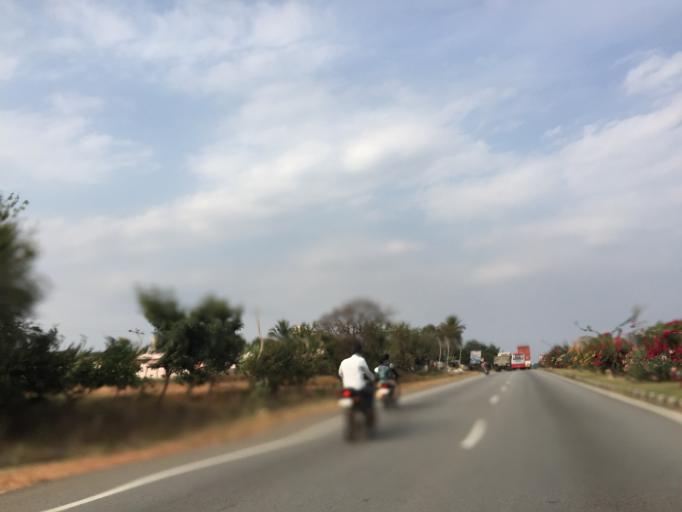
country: IN
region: Karnataka
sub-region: Chikkaballapur
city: Chik Ballapur
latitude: 13.4953
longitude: 77.7542
